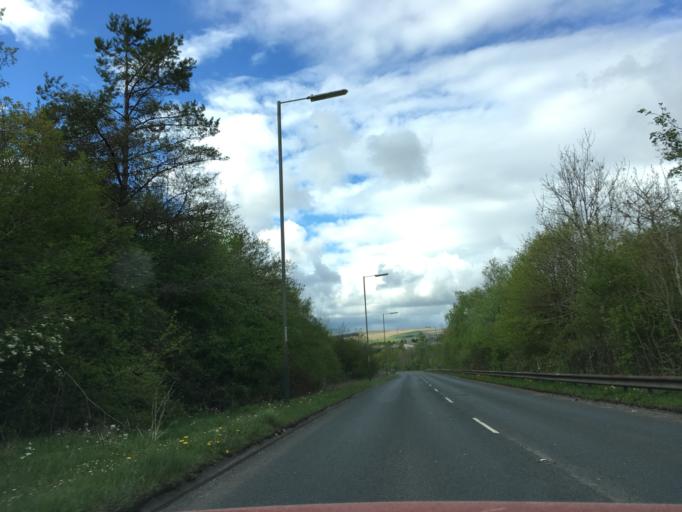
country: GB
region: Wales
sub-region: Caerphilly County Borough
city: Rhymney
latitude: 51.7589
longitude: -3.2909
